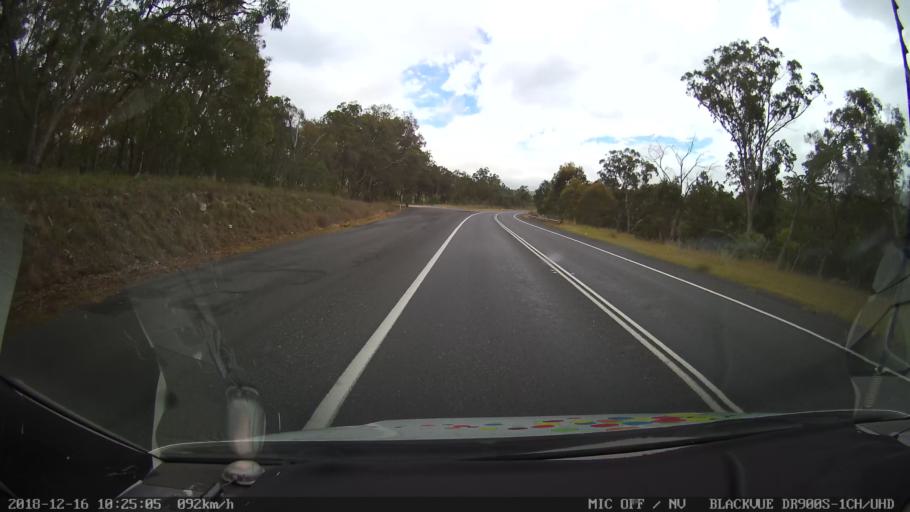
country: AU
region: New South Wales
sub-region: Tenterfield Municipality
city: Carrolls Creek
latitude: -29.1635
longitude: 152.0010
